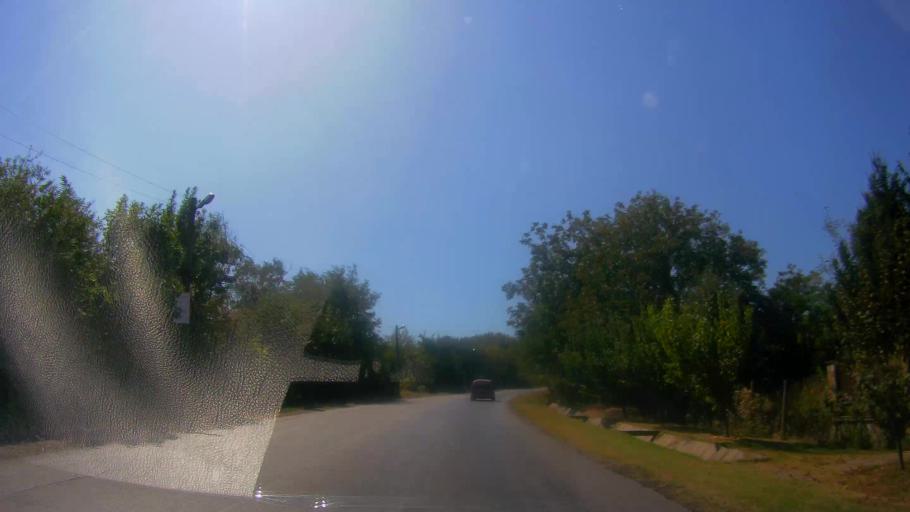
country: BG
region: Veliko Turnovo
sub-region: Obshtina Gorna Oryakhovitsa
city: Purvomaytsi
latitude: 43.1696
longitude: 25.6200
